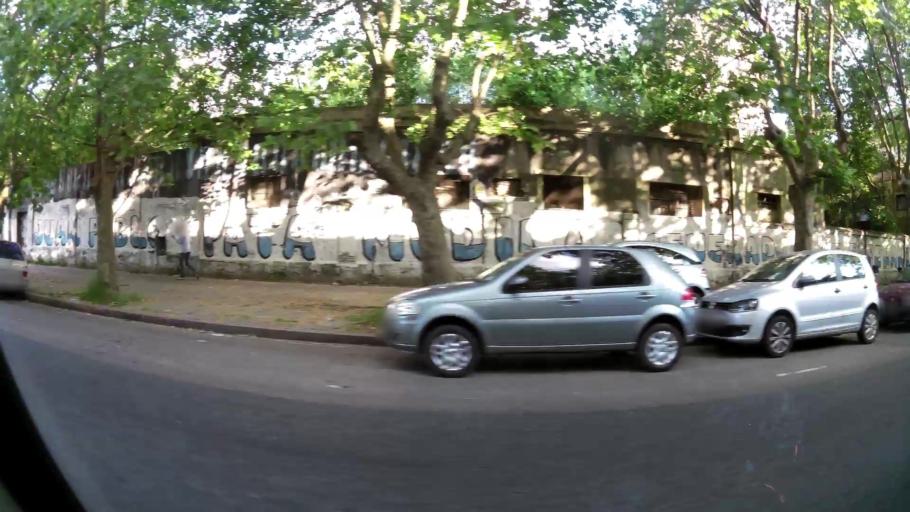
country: AR
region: Buenos Aires
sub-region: Partido de La Plata
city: La Plata
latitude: -34.9072
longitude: -57.9514
